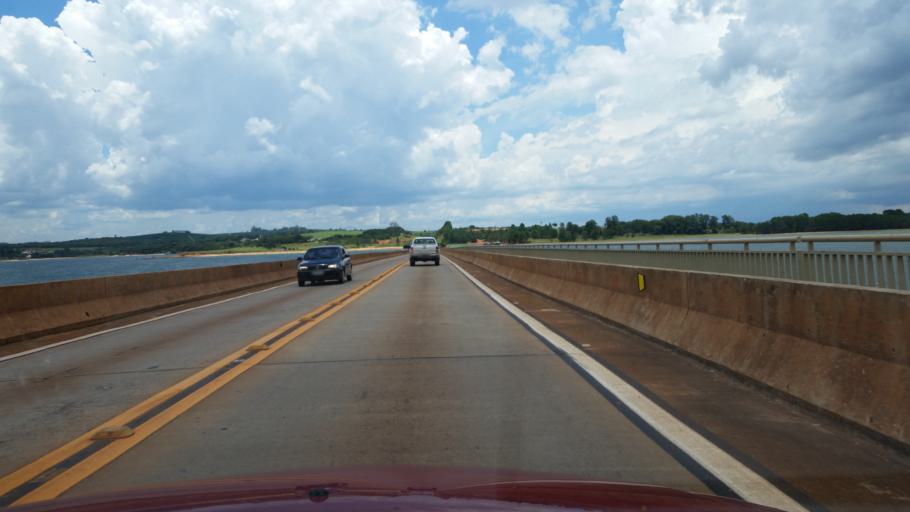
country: BR
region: Sao Paulo
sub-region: Itai
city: Itai
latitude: -23.2675
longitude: -49.0084
